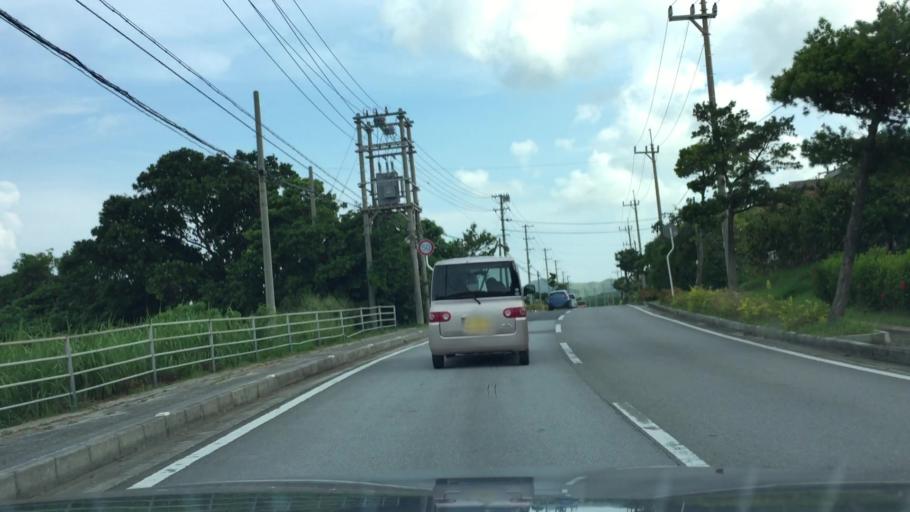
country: JP
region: Okinawa
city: Ishigaki
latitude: 24.4408
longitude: 124.2493
